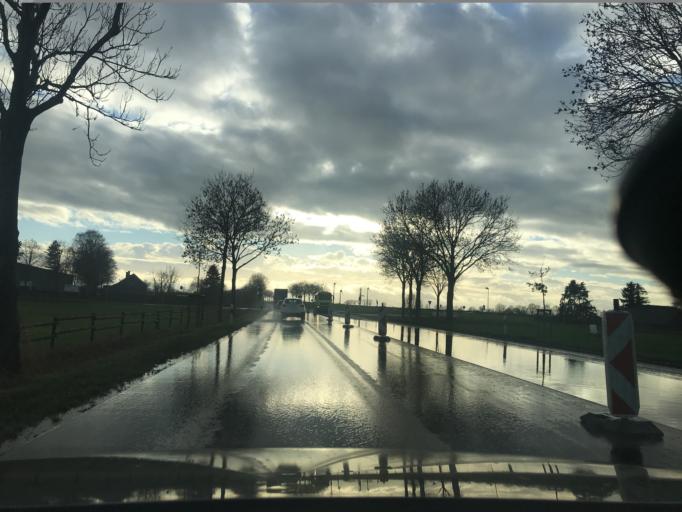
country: DE
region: North Rhine-Westphalia
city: Tonisvorst
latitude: 51.3899
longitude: 6.4924
